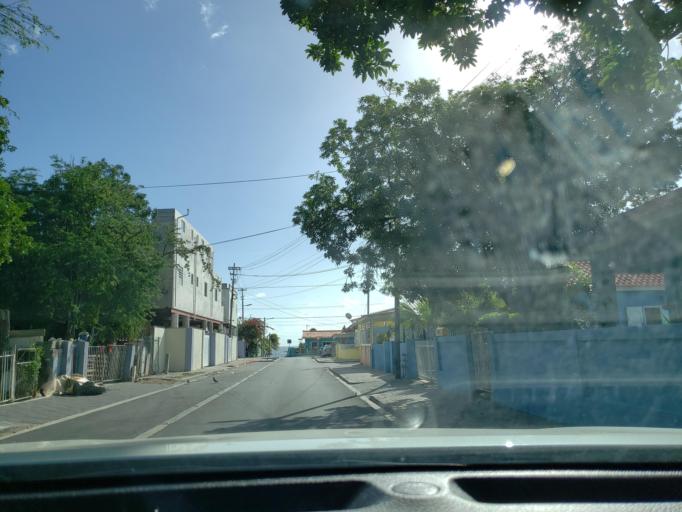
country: CW
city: Willemstad
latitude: 12.0978
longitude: -68.9146
